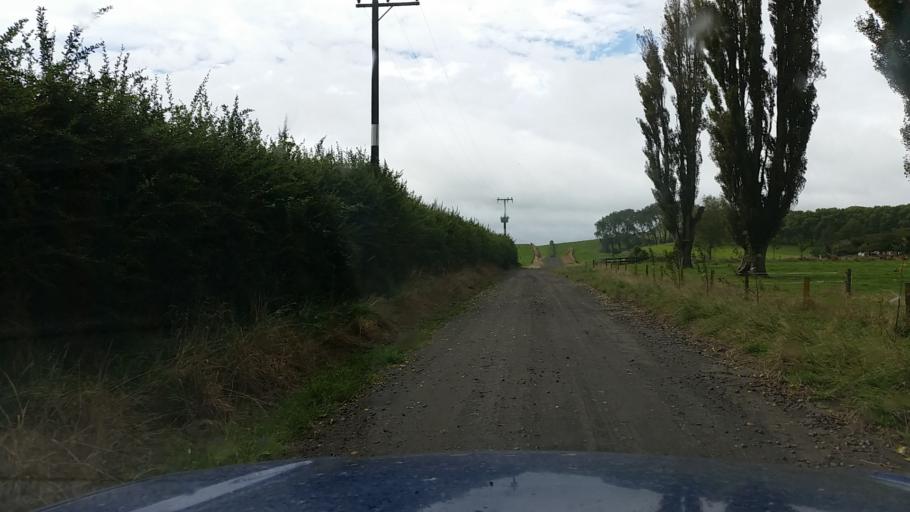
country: NZ
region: Taranaki
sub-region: South Taranaki District
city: Eltham
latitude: -39.3388
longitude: 174.4247
